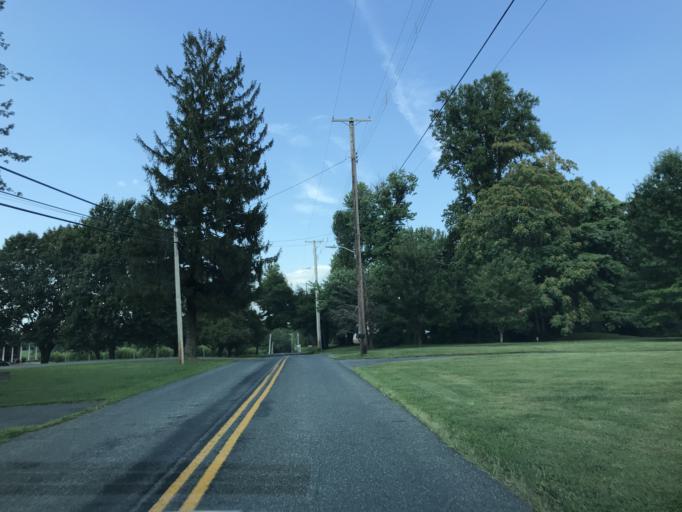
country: US
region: Maryland
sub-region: Harford County
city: South Bel Air
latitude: 39.6071
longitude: -76.3003
